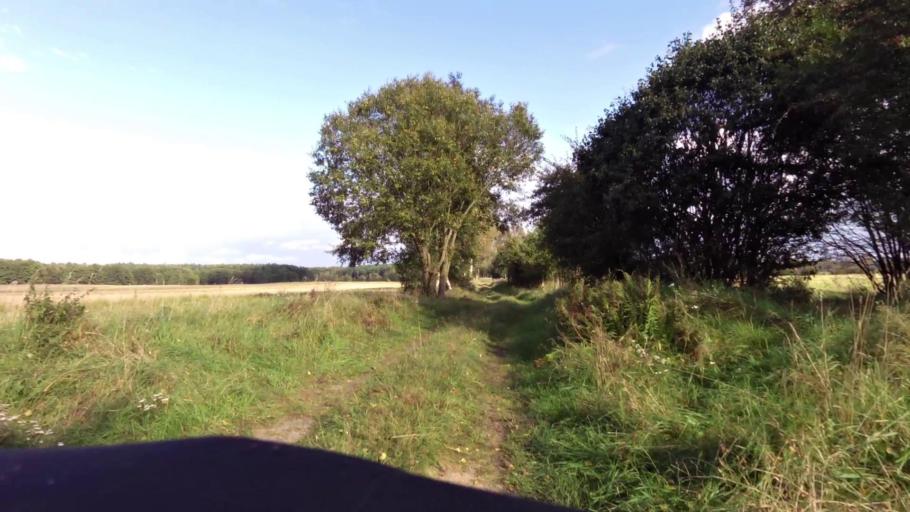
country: PL
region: West Pomeranian Voivodeship
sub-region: Powiat stargardzki
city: Marianowo
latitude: 53.3842
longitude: 15.3122
